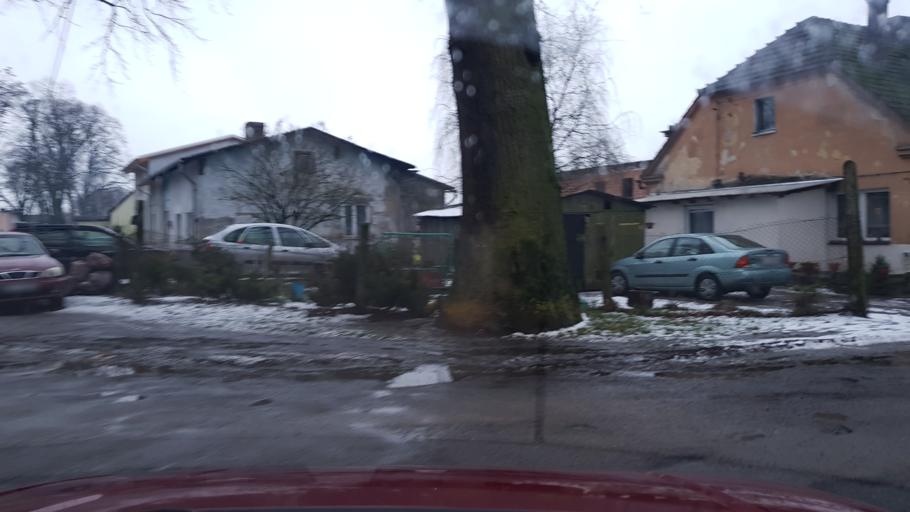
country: PL
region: West Pomeranian Voivodeship
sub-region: Powiat goleniowski
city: Mosty
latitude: 53.4983
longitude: 14.9430
